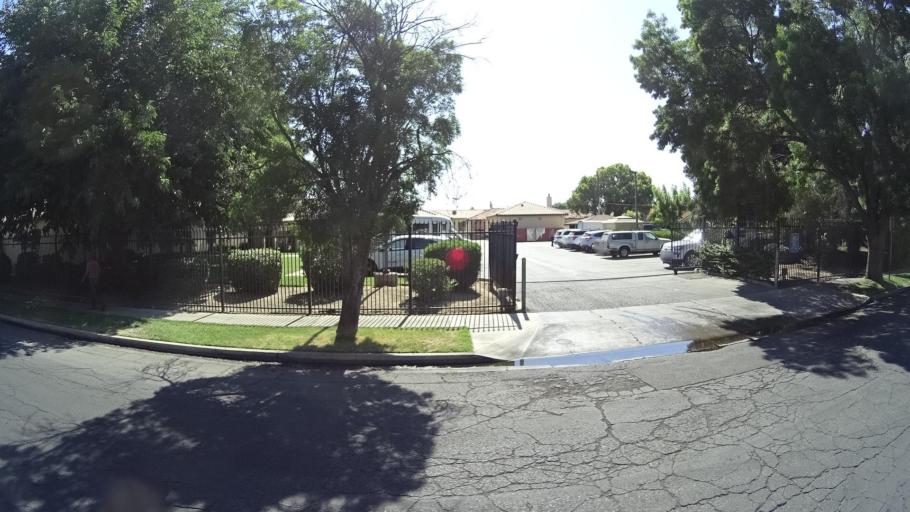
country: US
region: California
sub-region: Fresno County
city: Fresno
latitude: 36.7701
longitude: -119.7748
